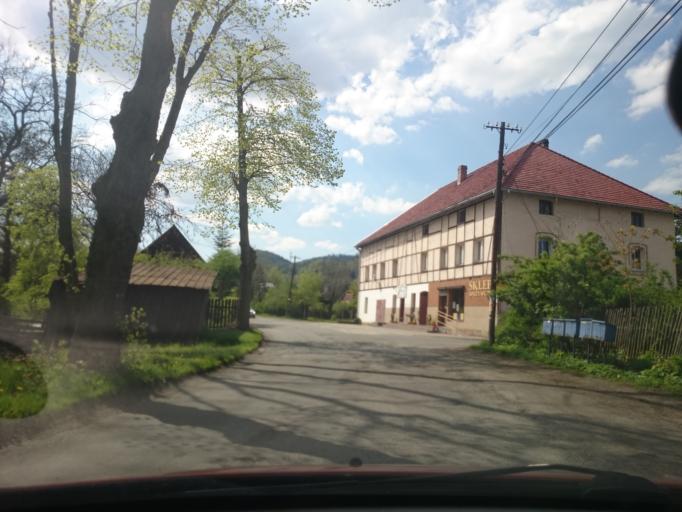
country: PL
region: Lower Silesian Voivodeship
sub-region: Powiat klodzki
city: Bystrzyca Klodzka
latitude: 50.3051
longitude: 16.6138
